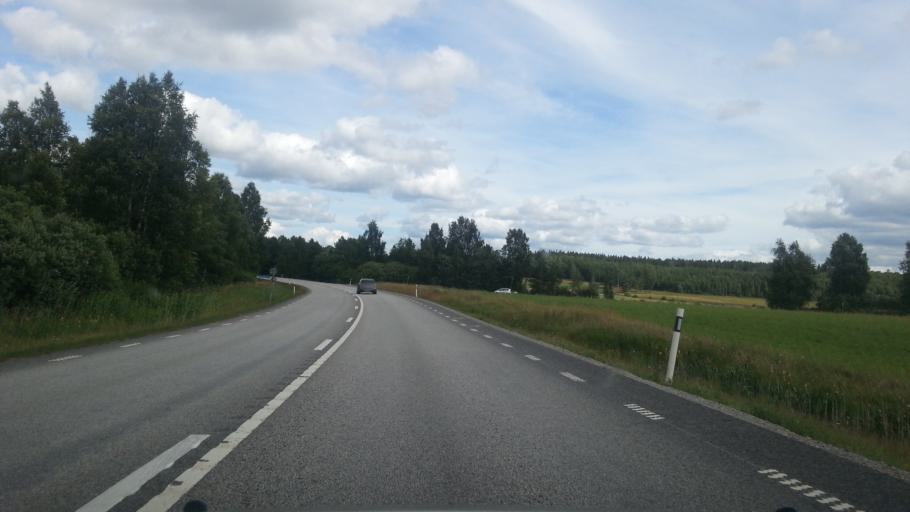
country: SE
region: OErebro
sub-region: Lindesbergs Kommun
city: Lindesberg
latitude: 59.6267
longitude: 15.2141
